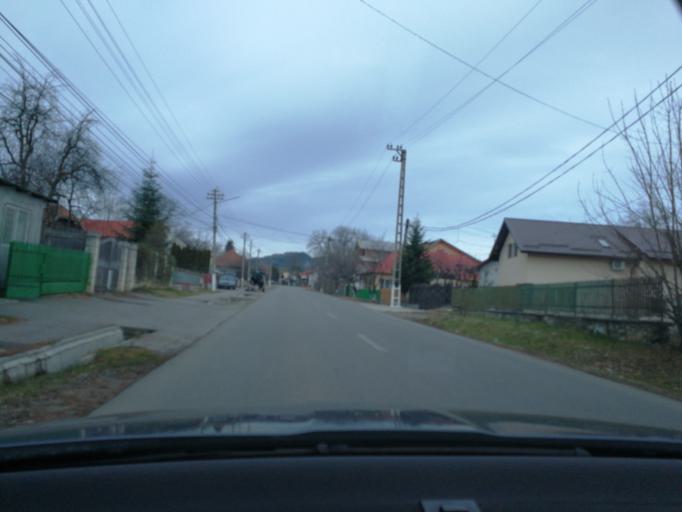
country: RO
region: Prahova
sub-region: Comuna Cornu
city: Cornu de Jos
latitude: 45.1516
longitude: 25.6885
